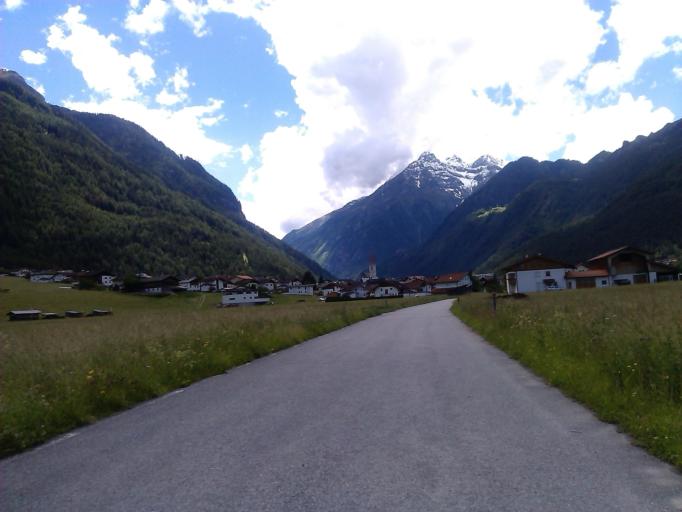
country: AT
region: Tyrol
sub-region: Politischer Bezirk Landeck
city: Pfunds
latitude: 46.9724
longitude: 10.5500
